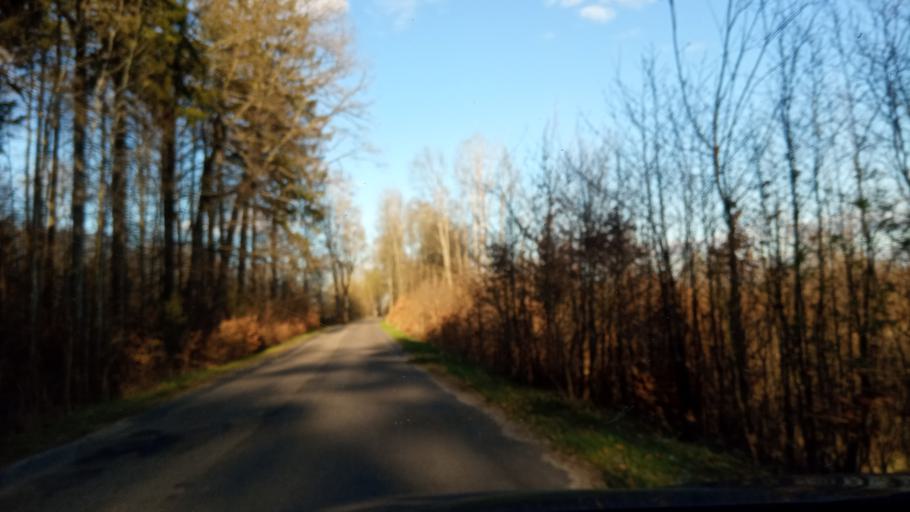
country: PL
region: West Pomeranian Voivodeship
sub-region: Powiat szczecinecki
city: Lubowo
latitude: 53.6033
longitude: 16.3166
